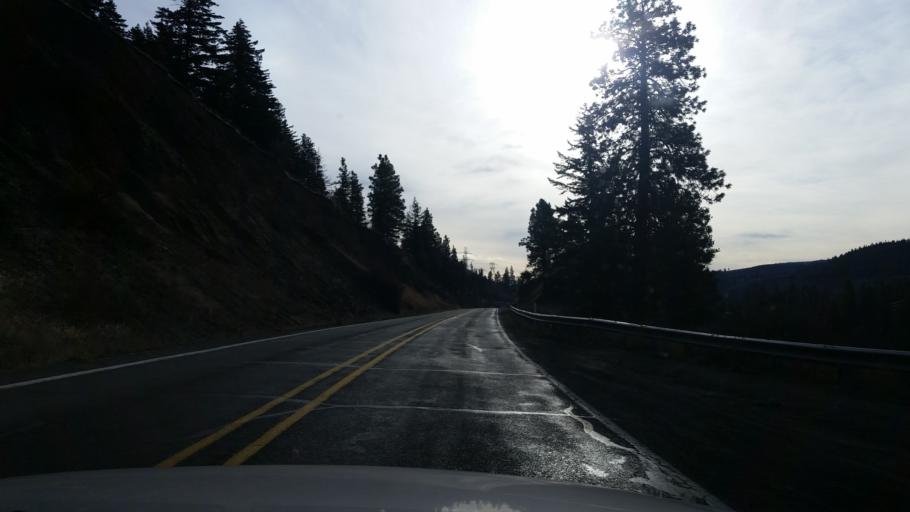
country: US
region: Washington
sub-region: Kittitas County
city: Cle Elum
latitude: 47.1641
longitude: -120.8112
